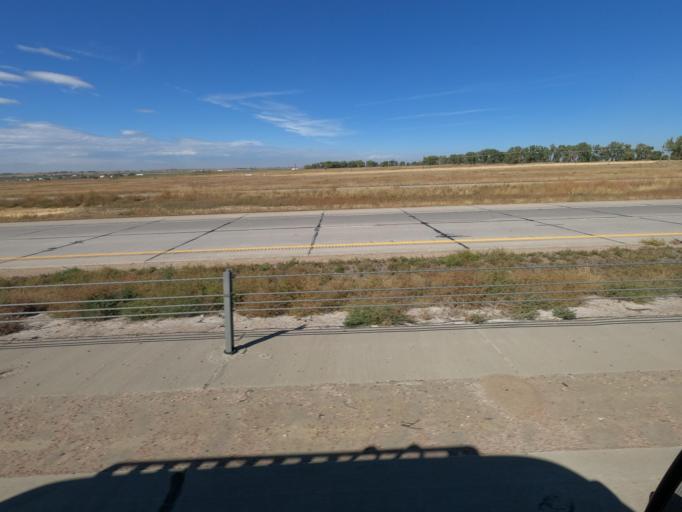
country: US
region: Colorado
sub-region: Weld County
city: Hudson
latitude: 40.0788
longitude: -104.6406
